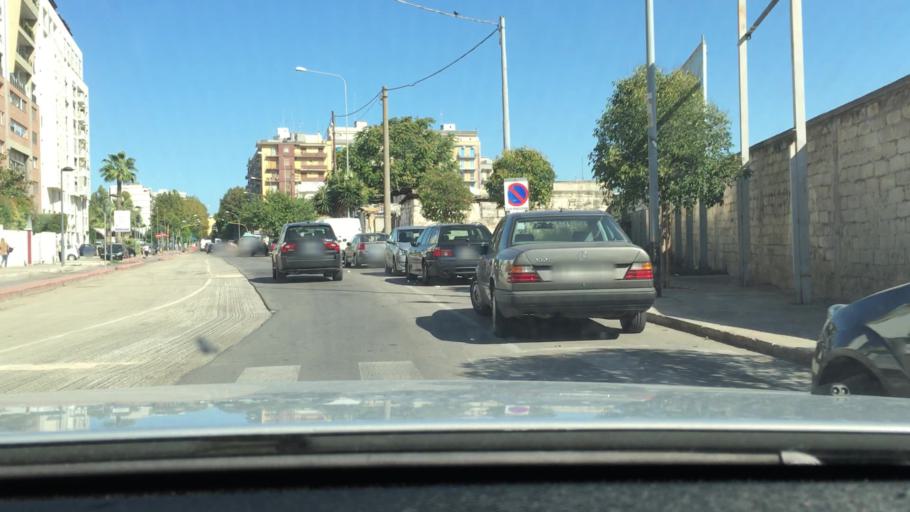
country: IT
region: Apulia
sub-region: Provincia di Bari
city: Bari
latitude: 41.1251
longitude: 16.8489
